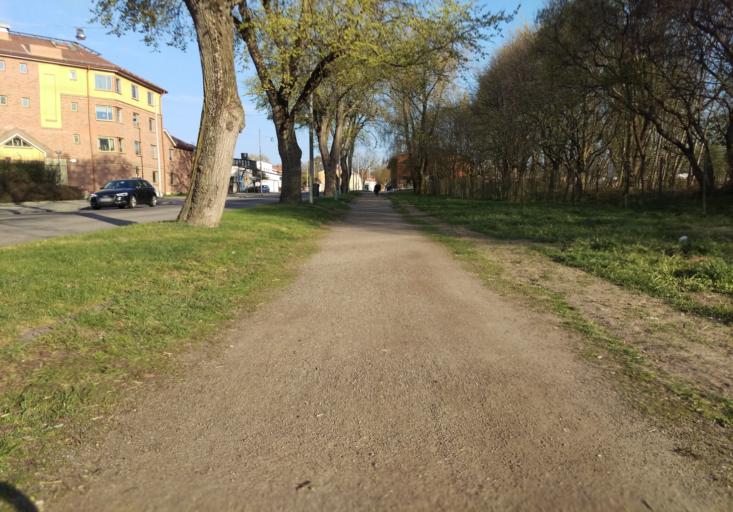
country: SE
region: OEstergoetland
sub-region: Norrkopings Kommun
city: Norrkoping
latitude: 58.5825
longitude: 16.2032
